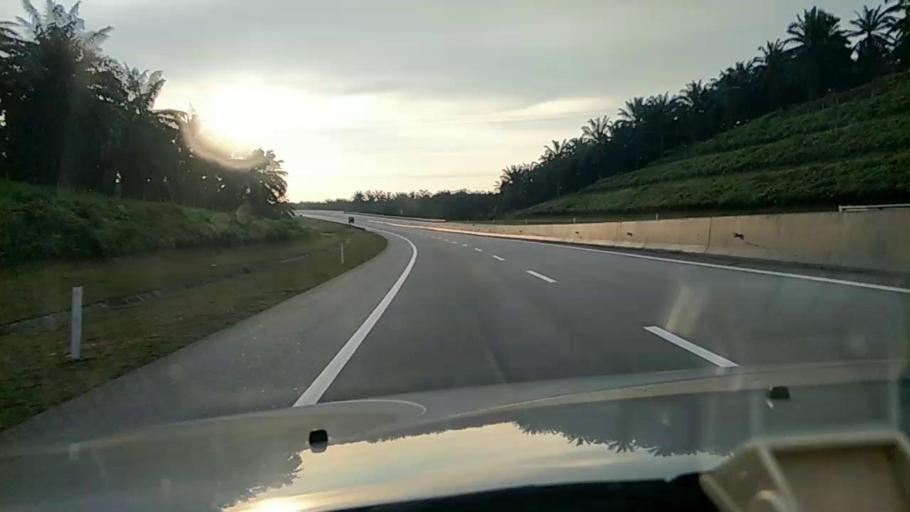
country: MY
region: Selangor
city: Batu Arang
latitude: 3.2874
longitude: 101.4376
